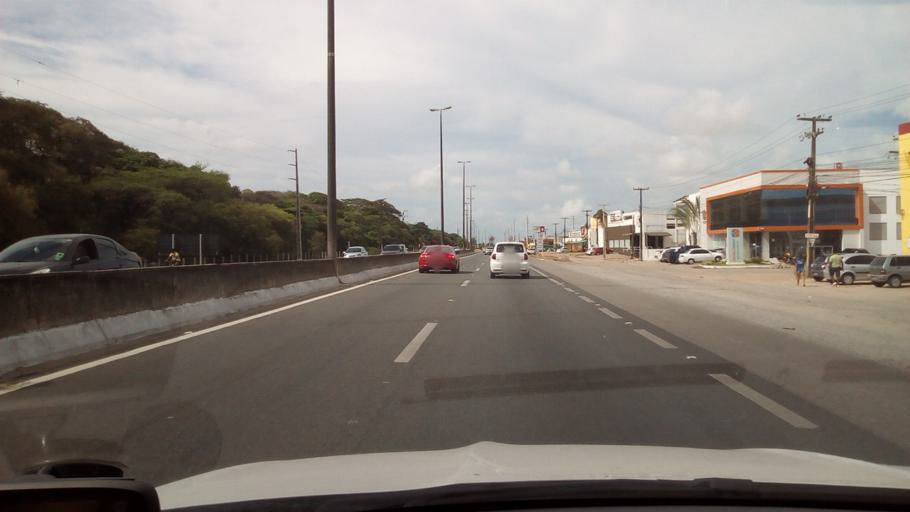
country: BR
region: Paraiba
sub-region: Joao Pessoa
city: Joao Pessoa
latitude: -7.0685
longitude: -34.8499
